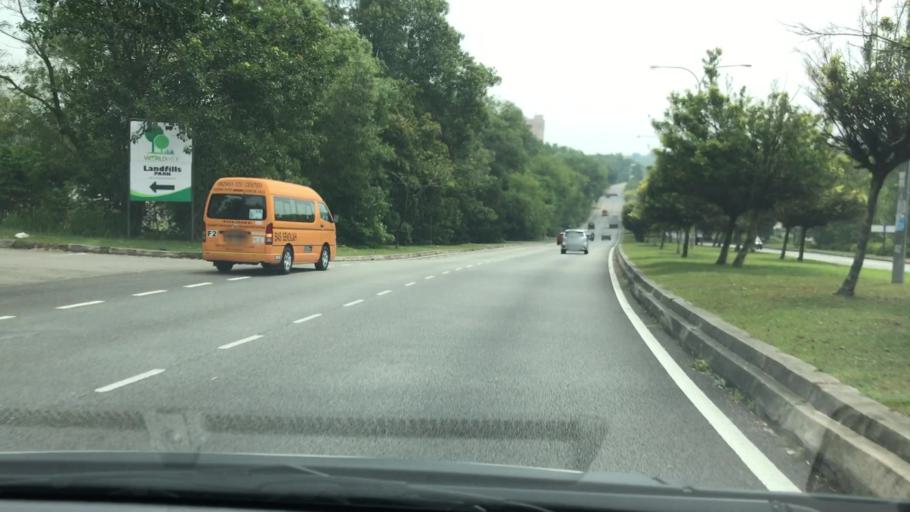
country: MY
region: Putrajaya
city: Putrajaya
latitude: 3.0015
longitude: 101.6649
